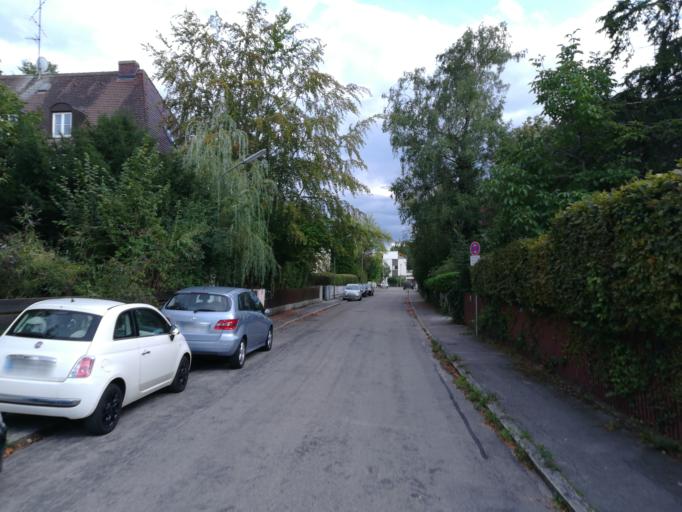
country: DE
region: Bavaria
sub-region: Upper Bavaria
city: Munich
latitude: 48.1619
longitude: 11.5207
